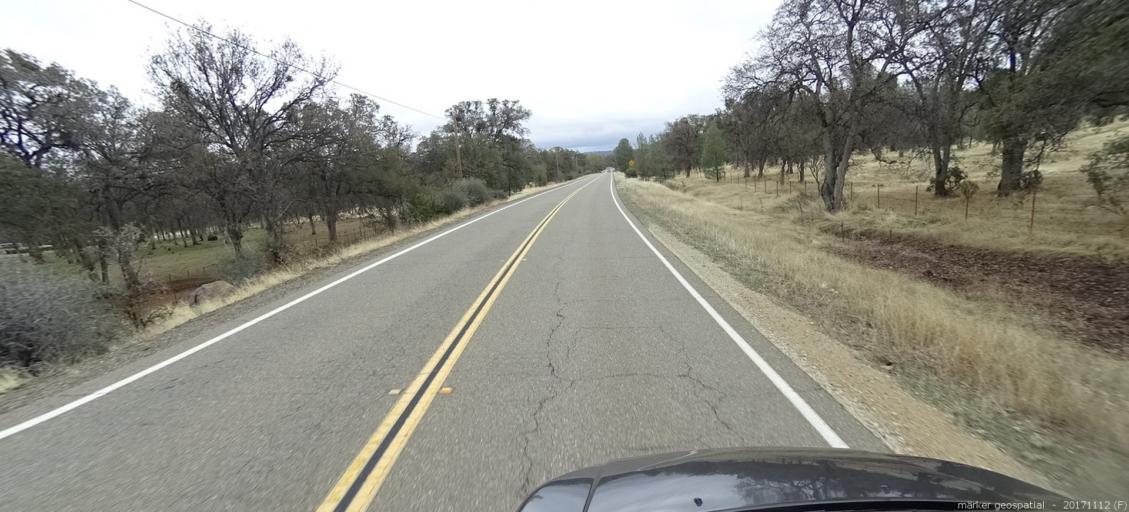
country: US
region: California
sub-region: Shasta County
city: Palo Cedro
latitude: 40.4858
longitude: -122.0772
